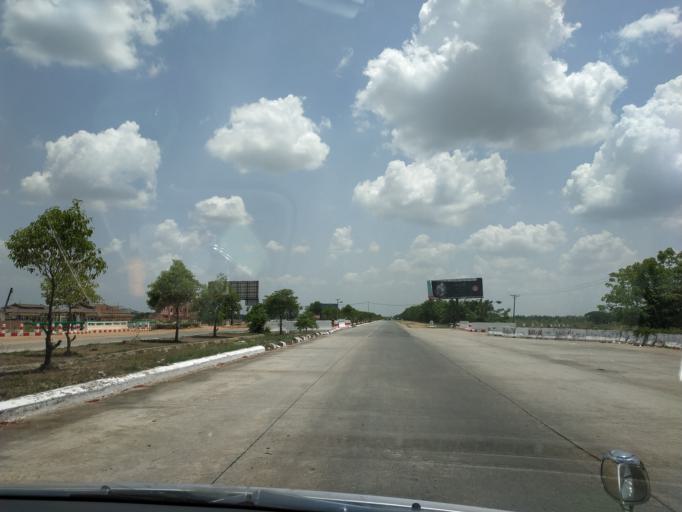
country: MM
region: Bago
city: Thanatpin
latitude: 17.0814
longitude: 96.1746
